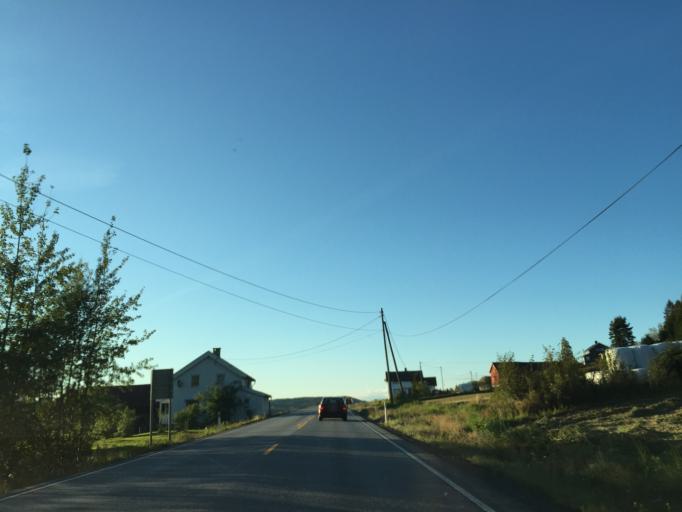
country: NO
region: Hedmark
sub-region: Nord-Odal
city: Sand
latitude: 60.3978
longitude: 11.5269
